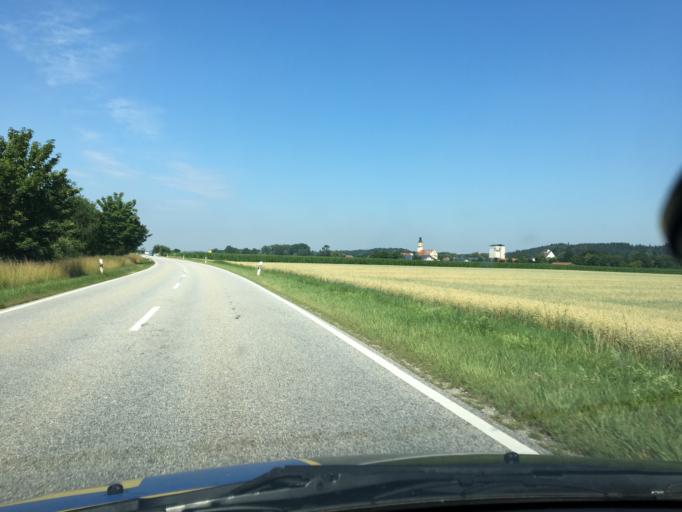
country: DE
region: Bavaria
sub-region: Upper Bavaria
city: Erharting
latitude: 48.2734
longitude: 12.5844
